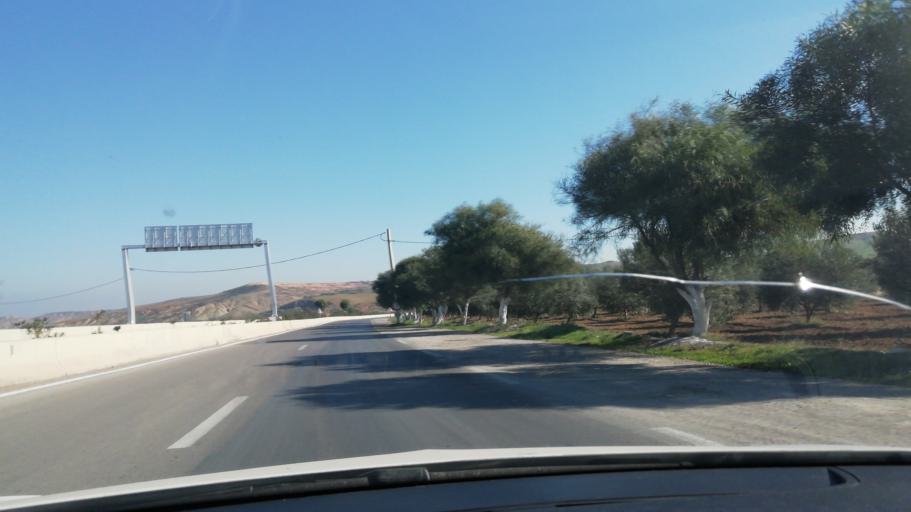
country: DZ
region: Tlemcen
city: Remchi
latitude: 35.0469
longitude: -1.5028
